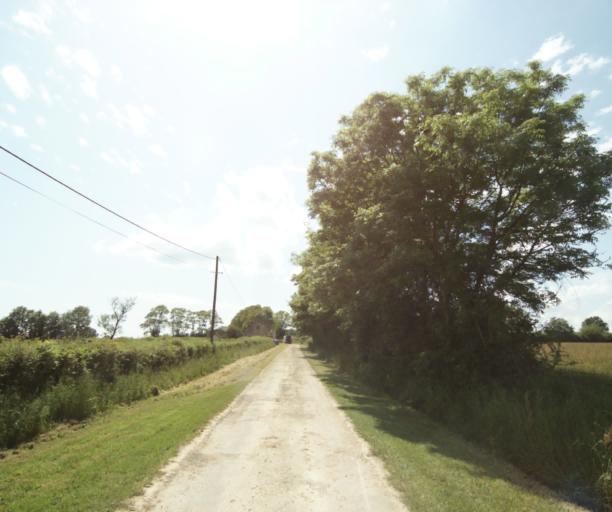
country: FR
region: Bourgogne
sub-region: Departement de Saone-et-Loire
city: Palinges
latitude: 46.5744
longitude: 4.1448
